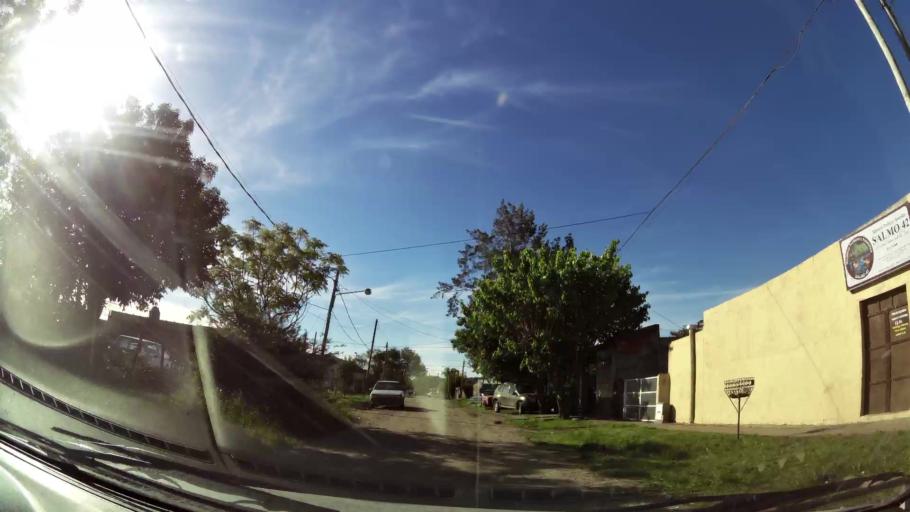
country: AR
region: Buenos Aires
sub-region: Partido de Almirante Brown
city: Adrogue
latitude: -34.8247
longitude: -58.3582
